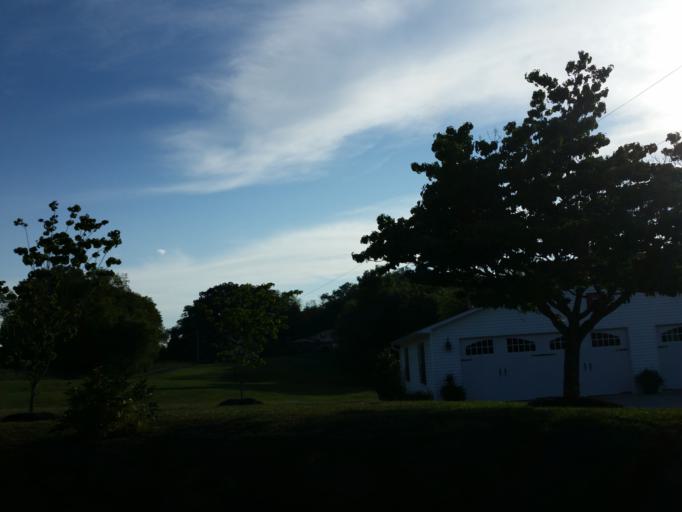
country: US
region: Tennessee
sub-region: Blount County
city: Eagleton Village
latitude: 35.8635
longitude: -83.9142
